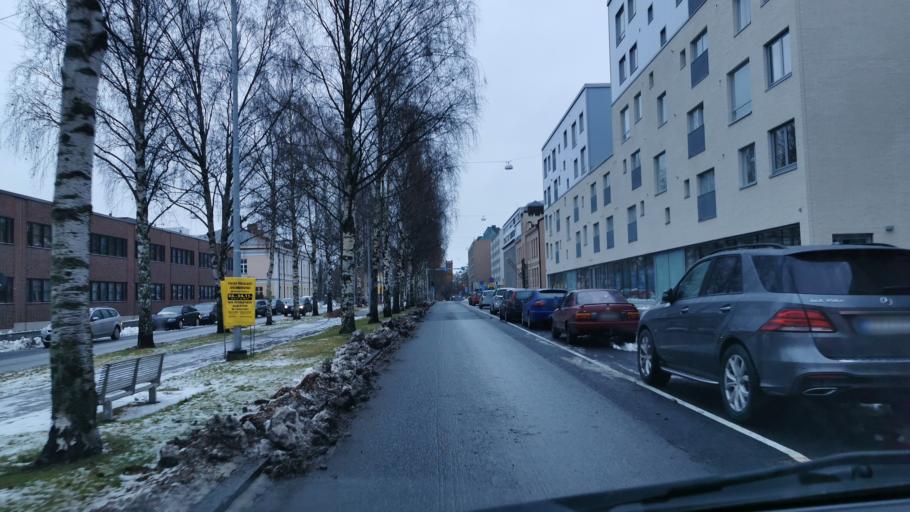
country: FI
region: Ostrobothnia
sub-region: Vaasa
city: Vaasa
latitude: 63.0981
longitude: 21.6070
